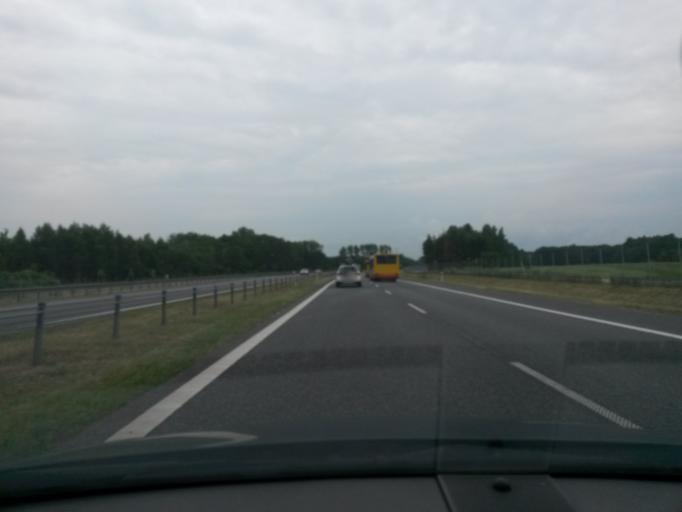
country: PL
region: Masovian Voivodeship
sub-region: Powiat zyrardowski
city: Mszczonow
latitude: 51.9615
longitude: 20.4990
